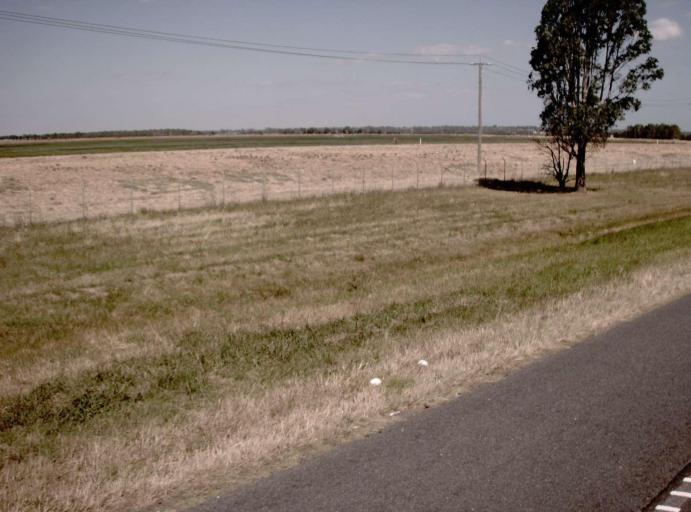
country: AU
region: Victoria
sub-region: Kingston
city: Patterson Lakes
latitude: -38.0611
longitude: 145.1484
